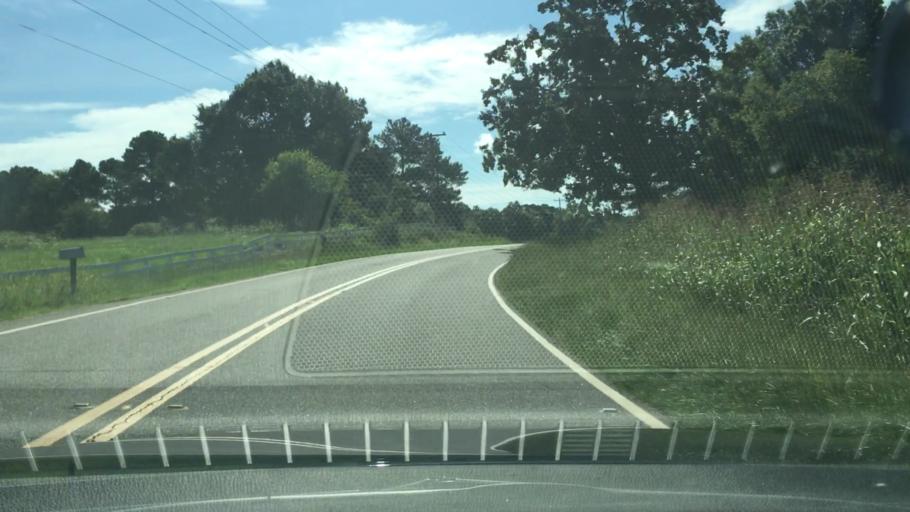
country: US
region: Georgia
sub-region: Putnam County
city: Jefferson
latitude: 33.4412
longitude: -83.3455
